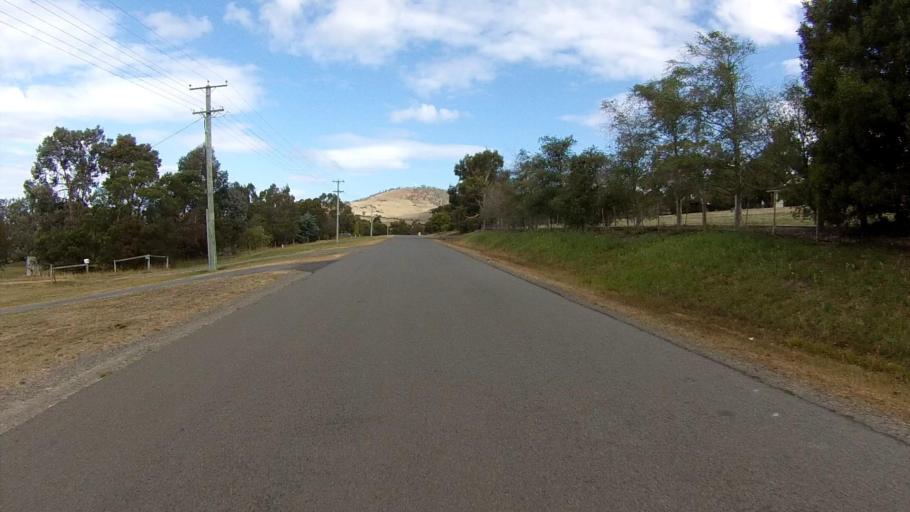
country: AU
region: Tasmania
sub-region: Clarence
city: Acton Park
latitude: -42.8589
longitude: 147.4832
